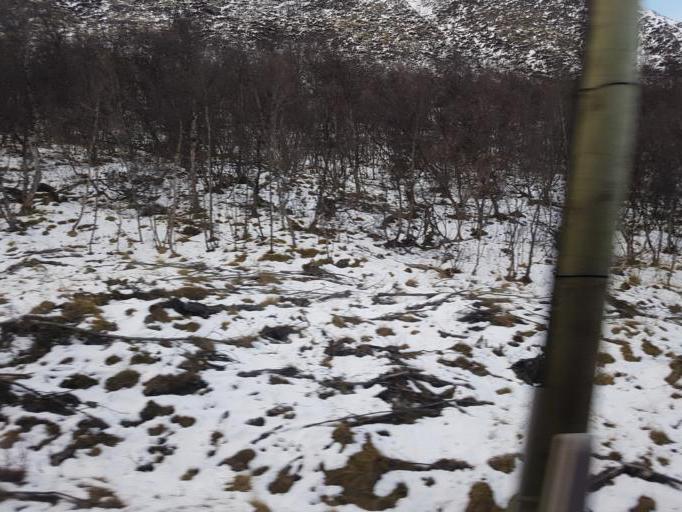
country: NO
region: Oppland
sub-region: Dovre
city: Dovre
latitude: 62.2164
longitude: 9.5496
